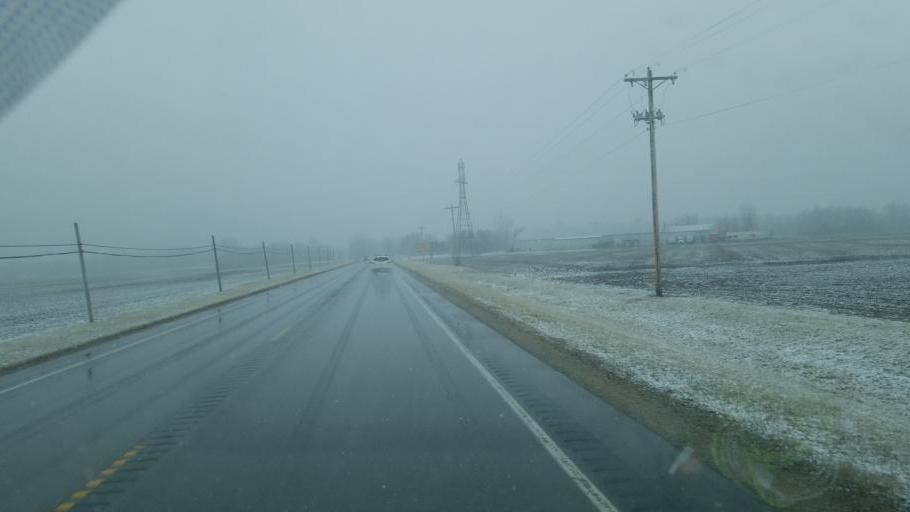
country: US
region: Indiana
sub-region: Grant County
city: Marion
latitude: 40.6224
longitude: -85.6995
